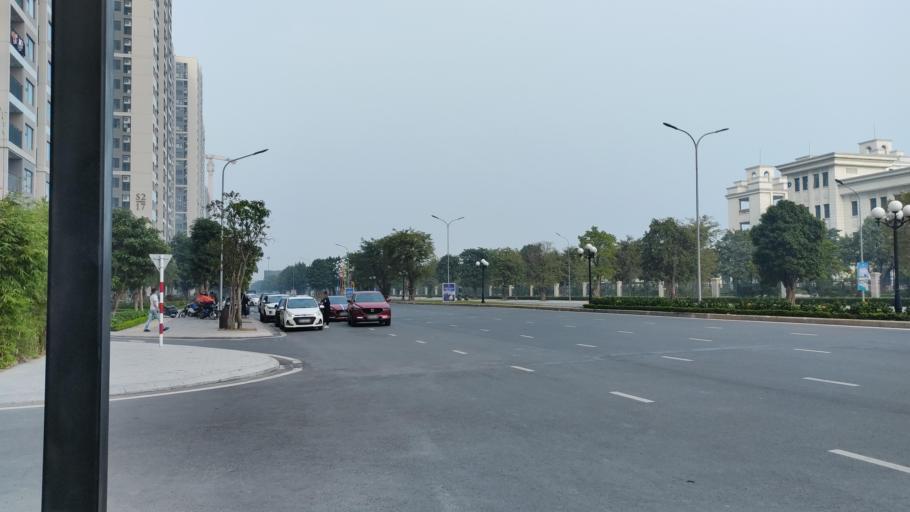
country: VN
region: Ha Noi
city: Trau Quy
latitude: 20.9891
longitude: 105.9425
